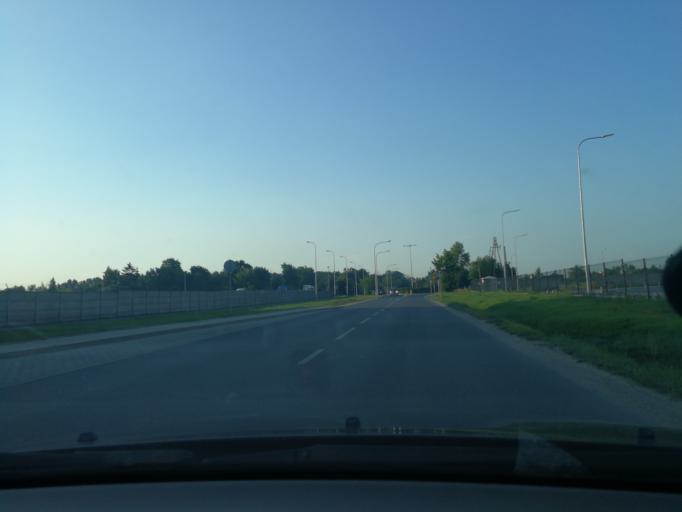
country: PL
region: Masovian Voivodeship
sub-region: Powiat pruszkowski
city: Brwinow
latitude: 52.1781
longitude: 20.7502
